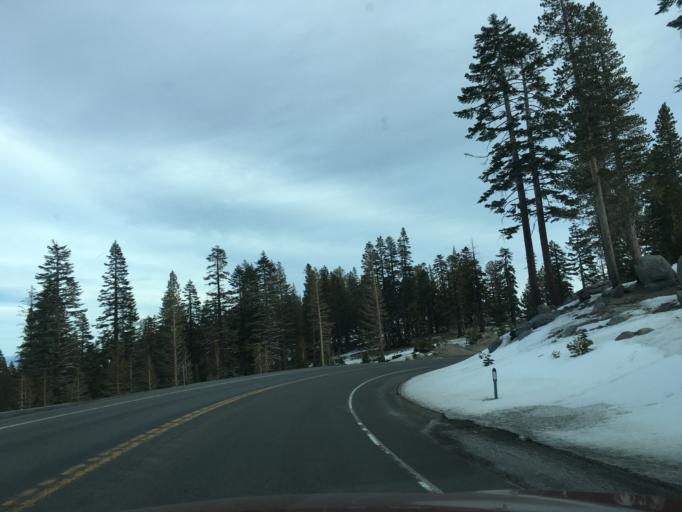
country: US
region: Nevada
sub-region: Washoe County
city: Incline Village
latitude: 39.3302
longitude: -119.8857
